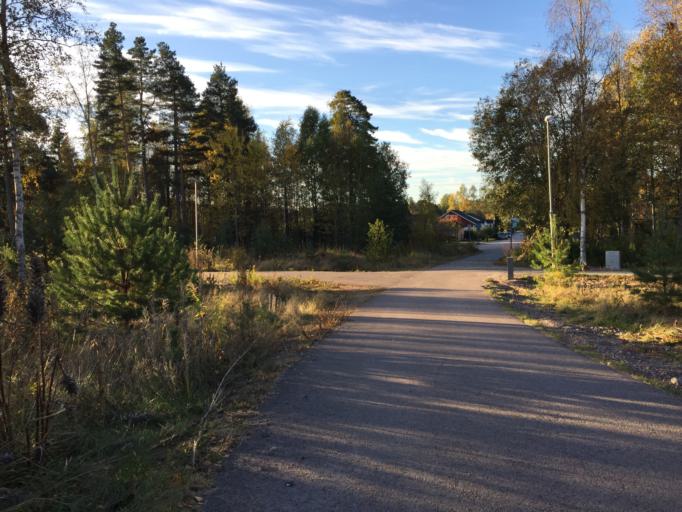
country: SE
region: Vaestmanland
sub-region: Hallstahammars Kommun
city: Hallstahammar
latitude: 59.6287
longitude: 16.2350
